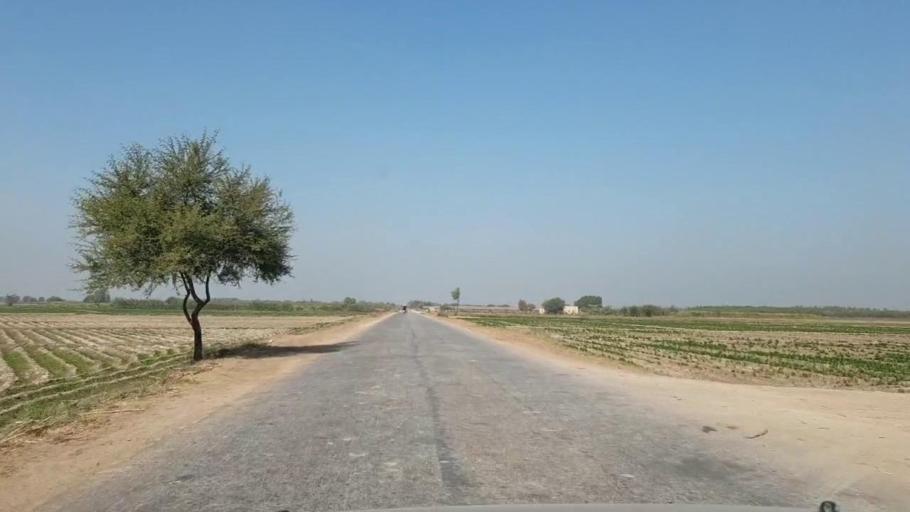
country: PK
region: Sindh
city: Tando Adam
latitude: 25.6613
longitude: 68.5838
